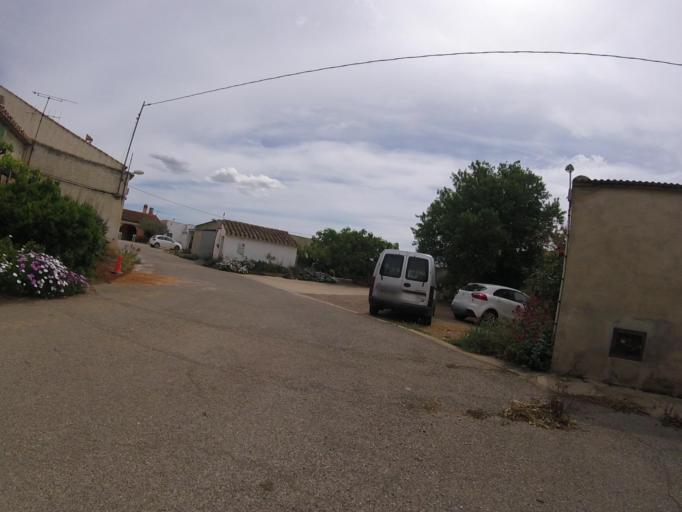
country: ES
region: Valencia
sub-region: Provincia de Castello
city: Benlloch
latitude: 40.1861
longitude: -0.0074
